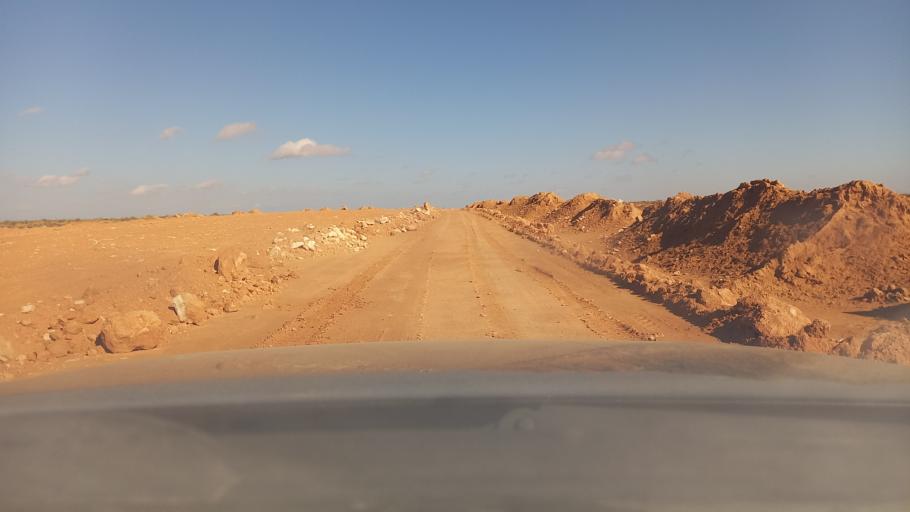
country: TN
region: Madanin
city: Medenine
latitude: 33.2432
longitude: 10.5583
